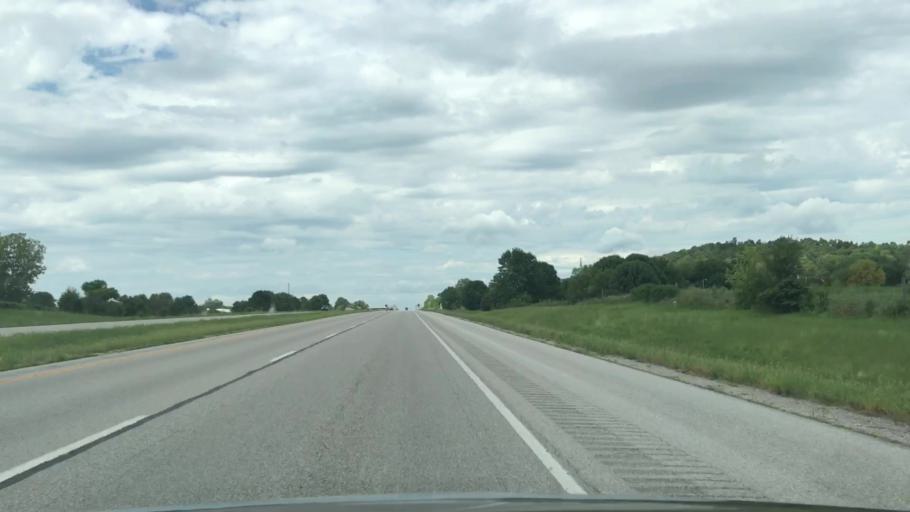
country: US
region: Kentucky
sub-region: Todd County
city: Elkton
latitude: 36.8220
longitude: -87.1930
